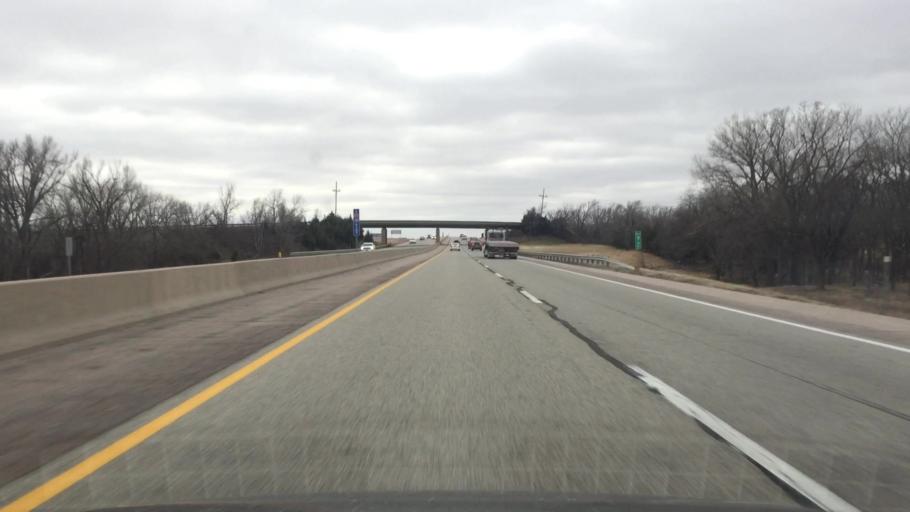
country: US
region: Kansas
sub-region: Butler County
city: El Dorado
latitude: 38.0446
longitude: -96.6436
